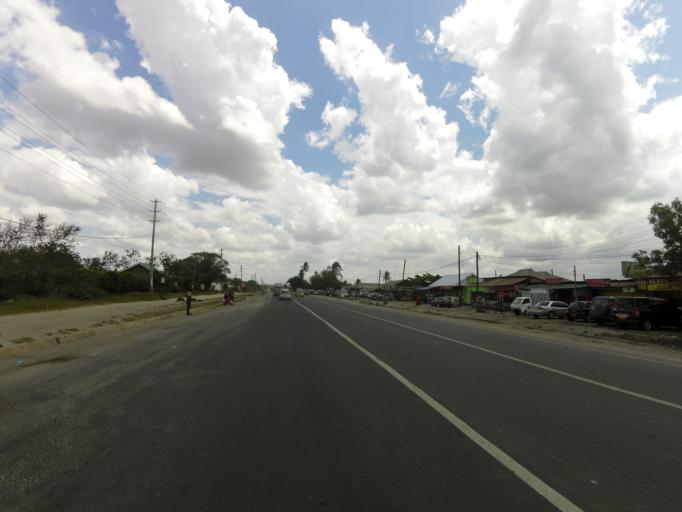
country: TZ
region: Dar es Salaam
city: Dar es Salaam
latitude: -6.8655
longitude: 39.2013
